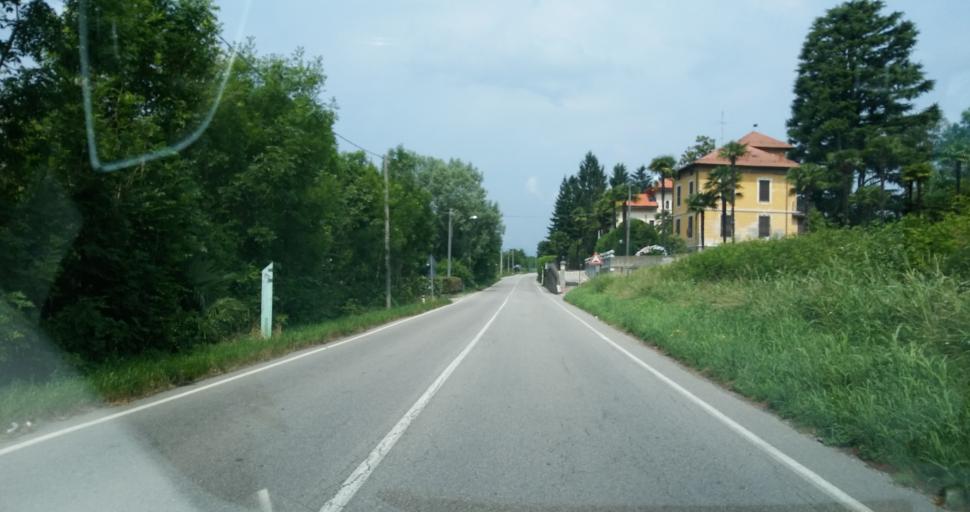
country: IT
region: Lombardy
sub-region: Provincia di Varese
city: Bardello
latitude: 45.8286
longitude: 8.7103
